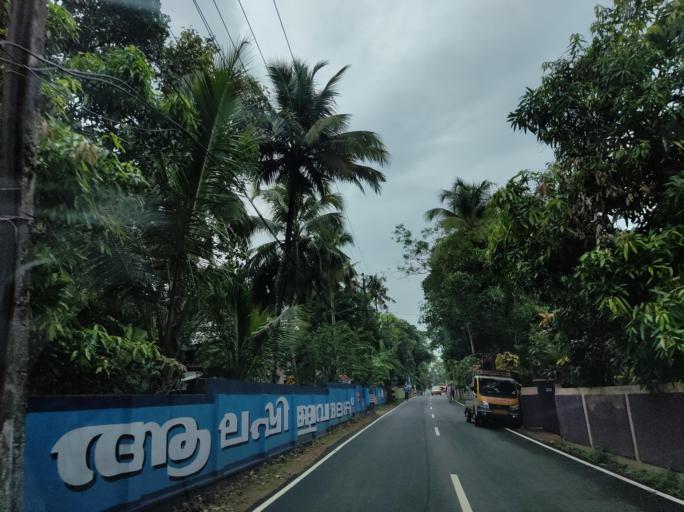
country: IN
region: Kerala
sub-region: Alappuzha
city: Mavelikara
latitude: 9.2430
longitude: 76.5520
